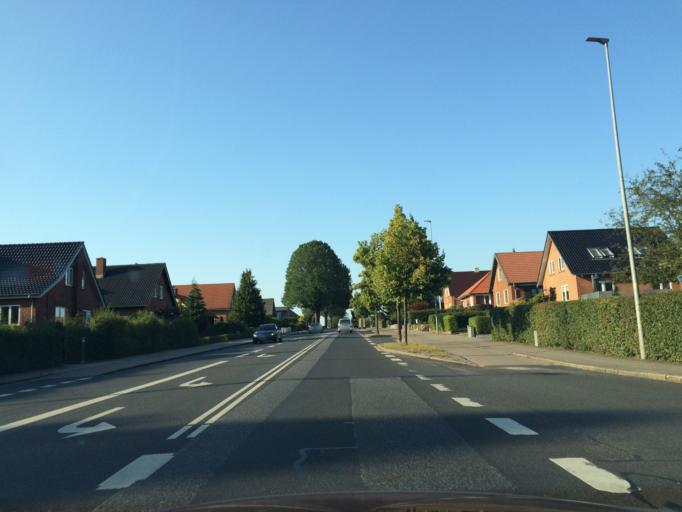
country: DK
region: Central Jutland
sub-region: Silkeborg Kommune
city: Silkeborg
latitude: 56.1569
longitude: 9.5495
